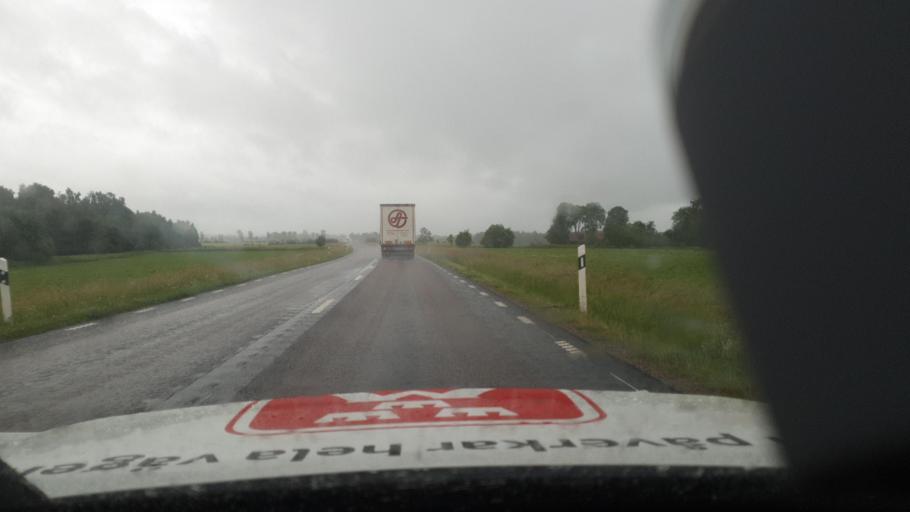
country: SE
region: Vaestra Goetaland
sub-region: Skovde Kommun
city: Skultorp
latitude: 58.2858
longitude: 13.7678
